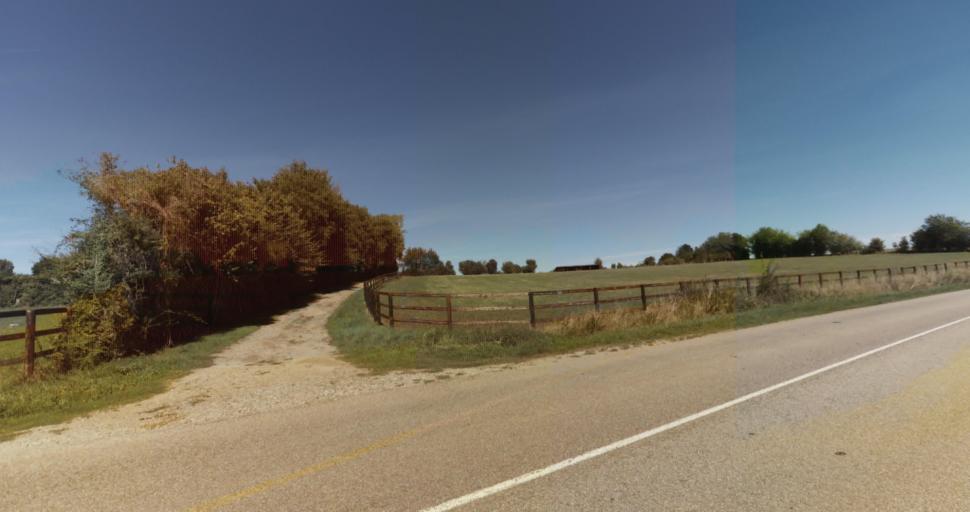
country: FR
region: Lower Normandy
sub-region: Departement de l'Orne
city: Gace
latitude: 48.7706
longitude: 0.2661
